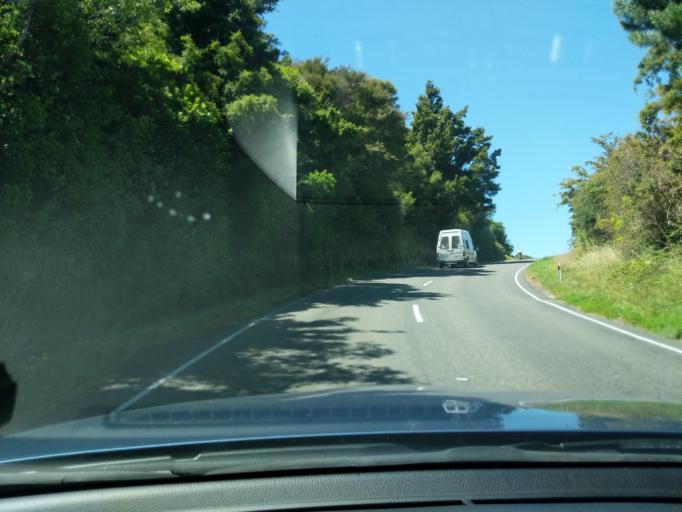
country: NZ
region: Tasman
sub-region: Tasman District
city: Takaka
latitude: -40.6955
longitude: 172.6334
